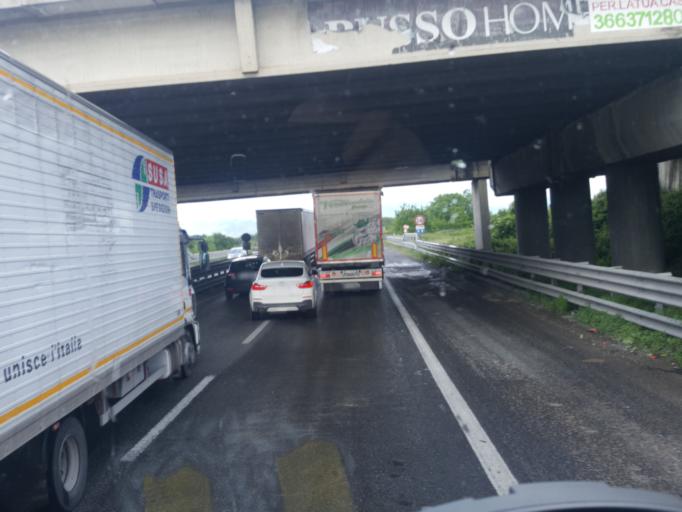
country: IT
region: Campania
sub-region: Provincia di Napoli
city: Pascarola
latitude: 40.9733
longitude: 14.2927
